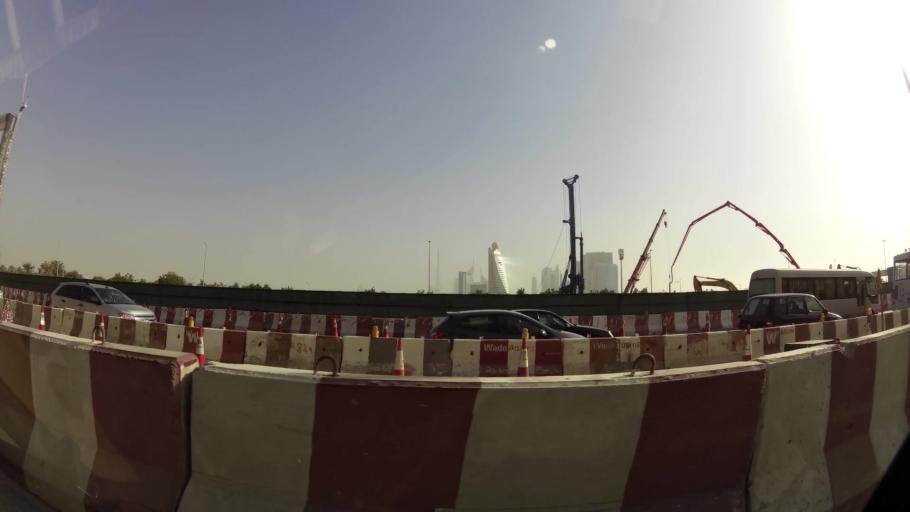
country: AE
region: Ash Shariqah
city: Sharjah
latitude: 25.2391
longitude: 55.2973
